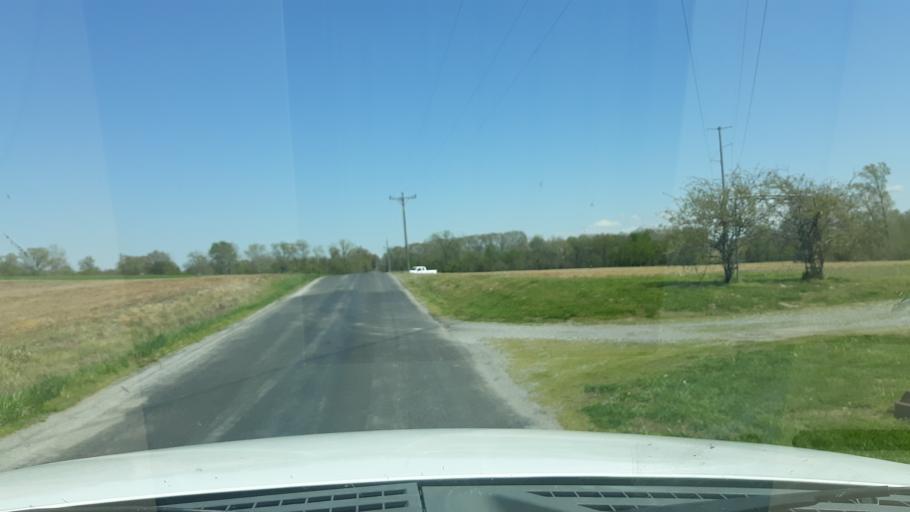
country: US
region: Illinois
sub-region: Saline County
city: Harrisburg
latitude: 37.8341
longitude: -88.6243
